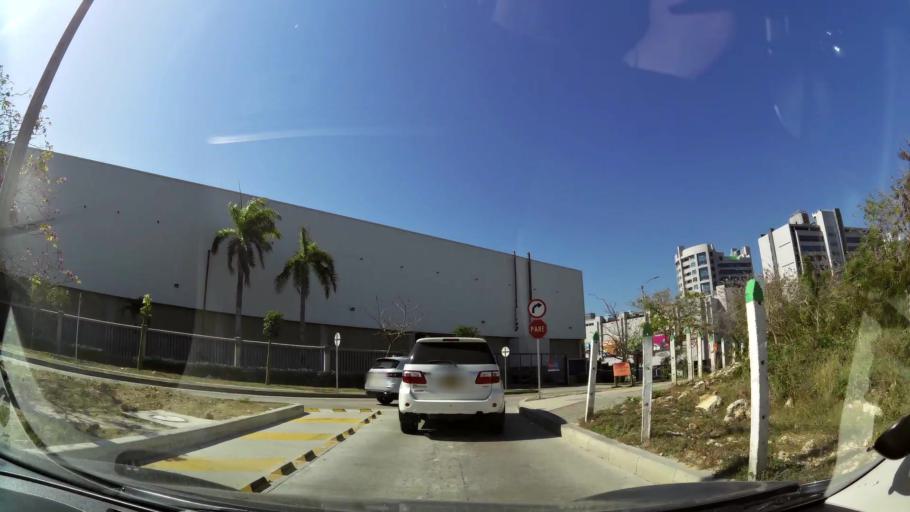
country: CO
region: Atlantico
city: Barranquilla
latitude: 11.0166
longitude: -74.8295
